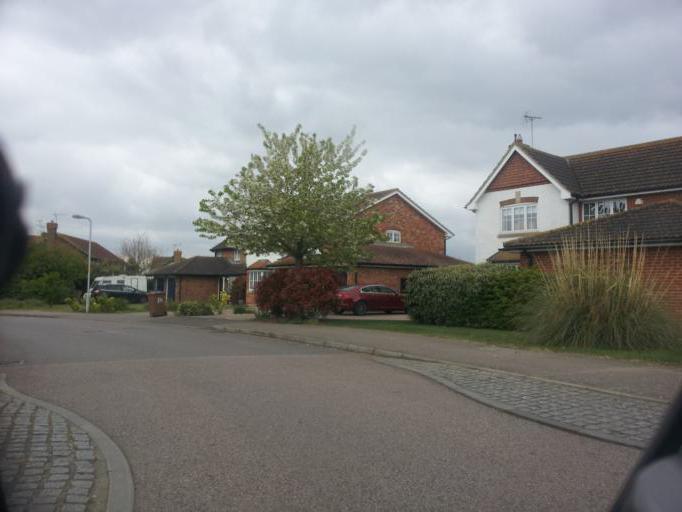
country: GB
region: England
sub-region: Kent
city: Leysdown-on-Sea
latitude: 51.4144
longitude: 0.8424
